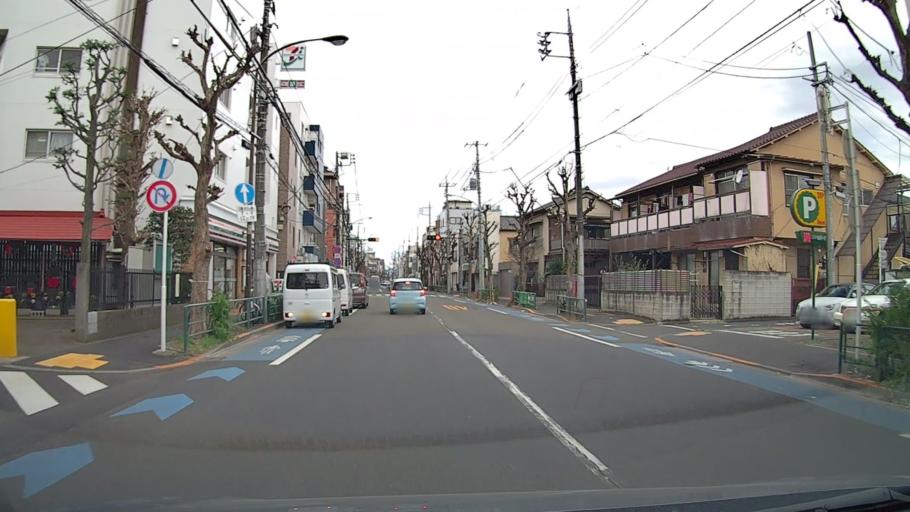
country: JP
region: Tokyo
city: Tokyo
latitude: 35.7124
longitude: 139.6403
